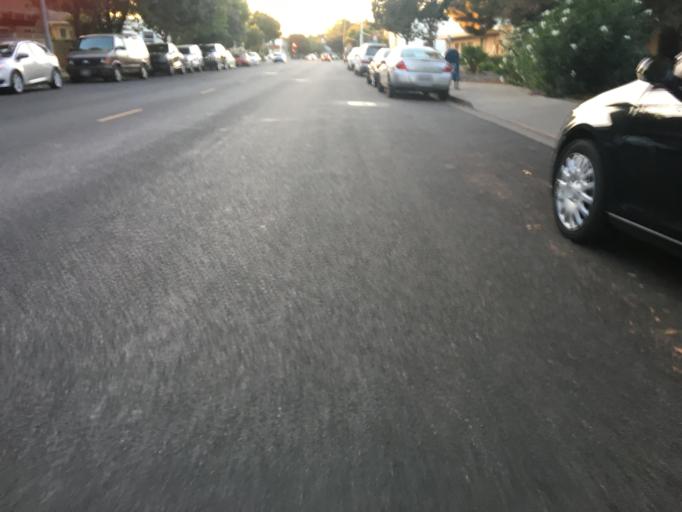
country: US
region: California
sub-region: Santa Clara County
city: Mountain View
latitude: 37.3971
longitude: -122.0749
